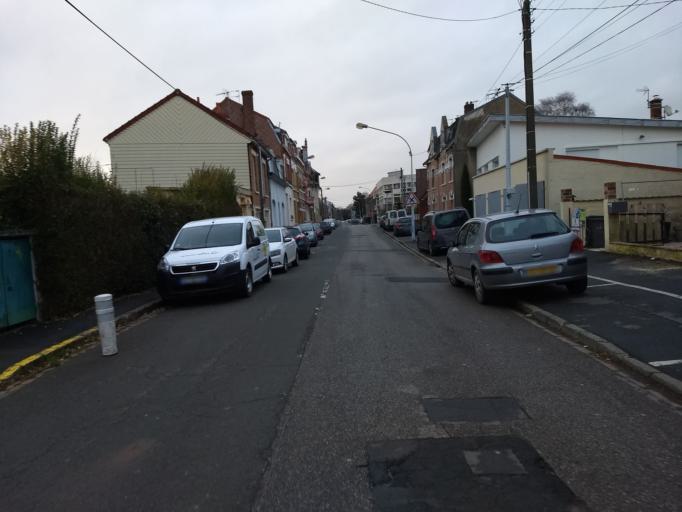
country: FR
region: Nord-Pas-de-Calais
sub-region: Departement du Pas-de-Calais
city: Achicourt
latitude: 50.2812
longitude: 2.7662
